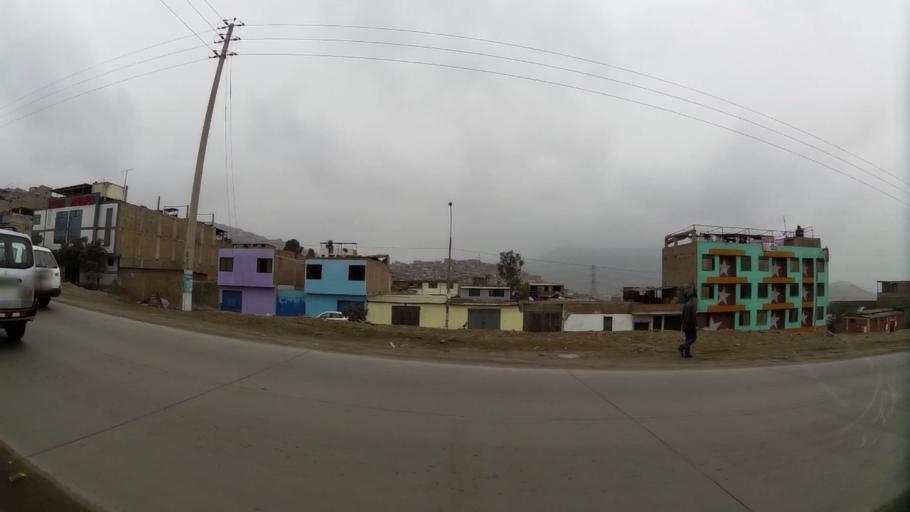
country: PE
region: Lima
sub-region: Lima
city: Surco
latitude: -12.2273
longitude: -76.9153
